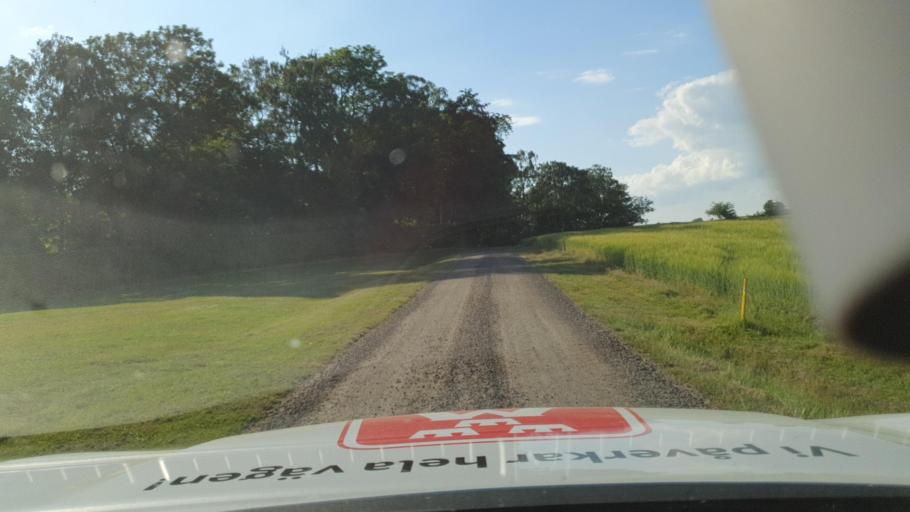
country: SE
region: Skane
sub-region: Skurups Kommun
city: Rydsgard
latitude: 55.4903
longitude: 13.5774
